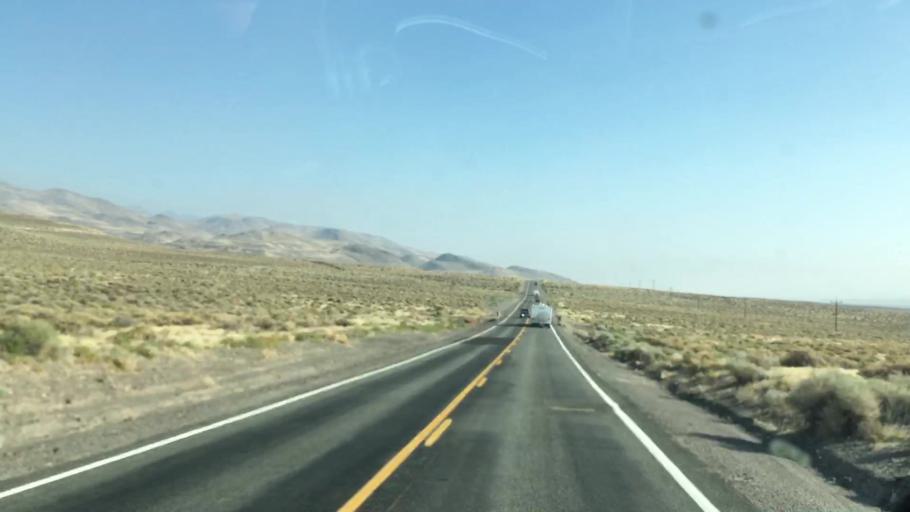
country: US
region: Nevada
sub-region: Lyon County
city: Fernley
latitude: 40.0220
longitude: -119.3869
